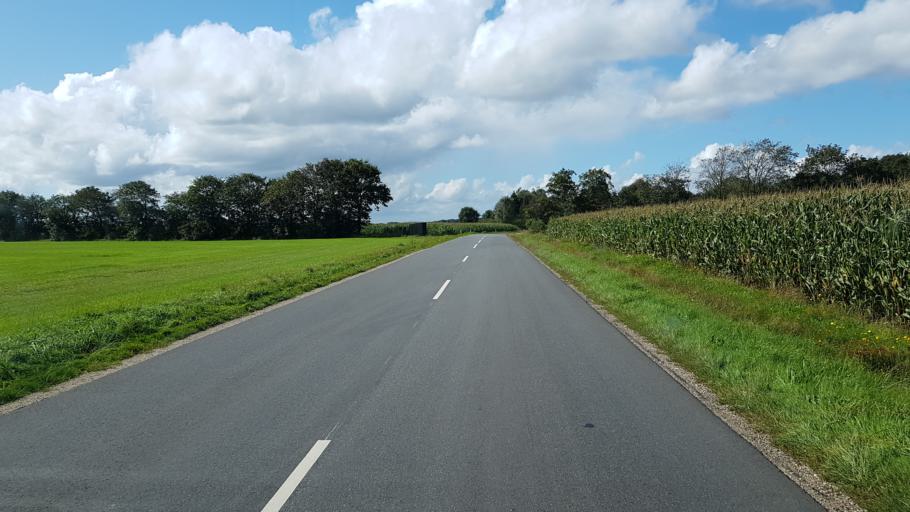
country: DK
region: South Denmark
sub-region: Esbjerg Kommune
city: Bramming
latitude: 55.6148
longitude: 8.7546
